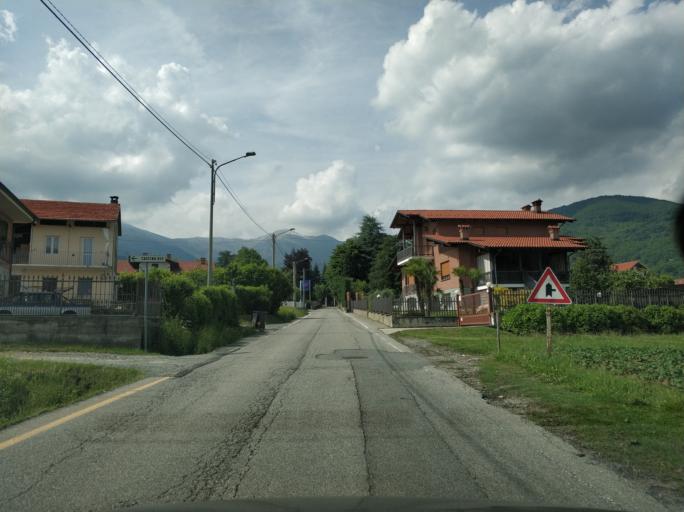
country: IT
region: Piedmont
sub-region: Provincia di Torino
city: Corio
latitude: 45.3074
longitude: 7.5373
